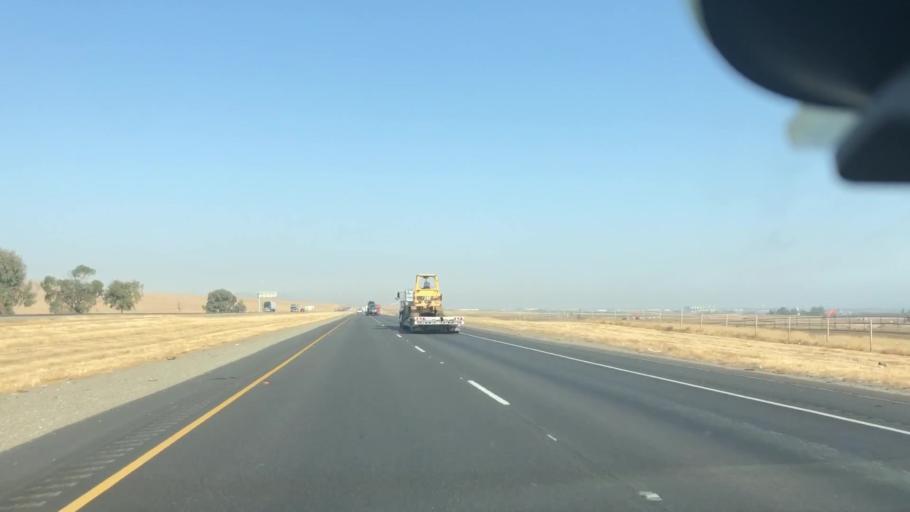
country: US
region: California
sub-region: San Joaquin County
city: Tracy
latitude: 37.6785
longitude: -121.4674
